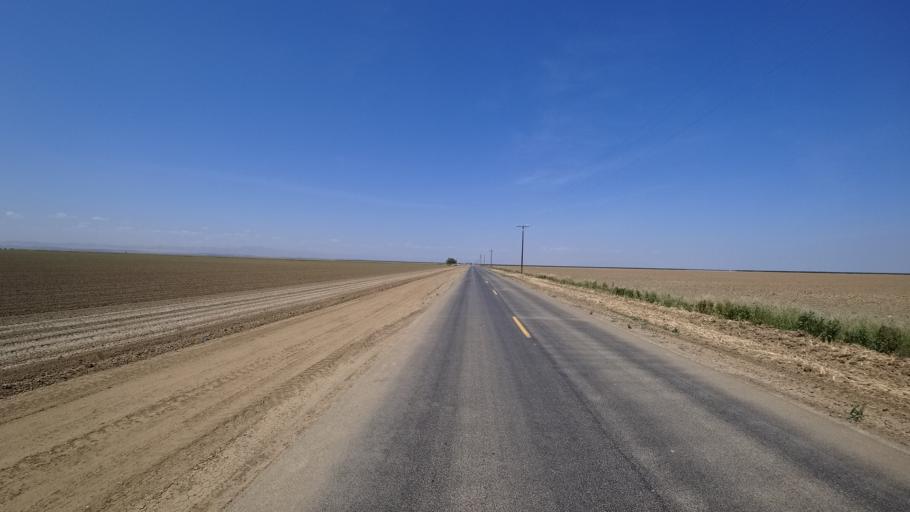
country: US
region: California
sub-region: Kings County
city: Stratford
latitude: 36.1377
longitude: -119.9365
